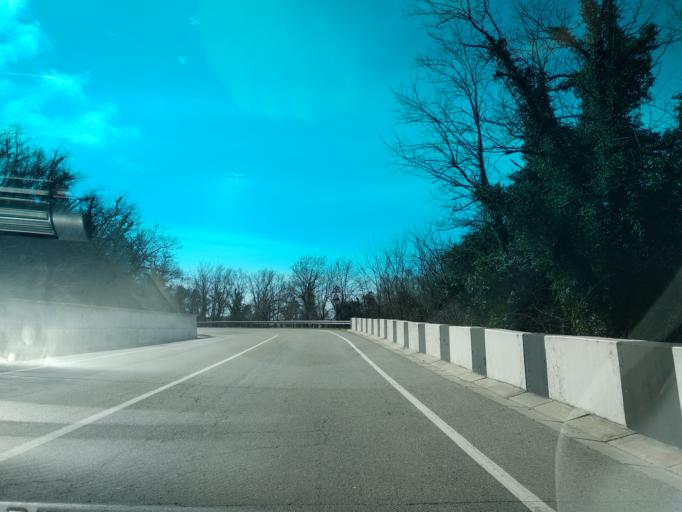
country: RU
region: Krasnodarskiy
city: Tuapse
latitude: 44.0910
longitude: 39.1186
